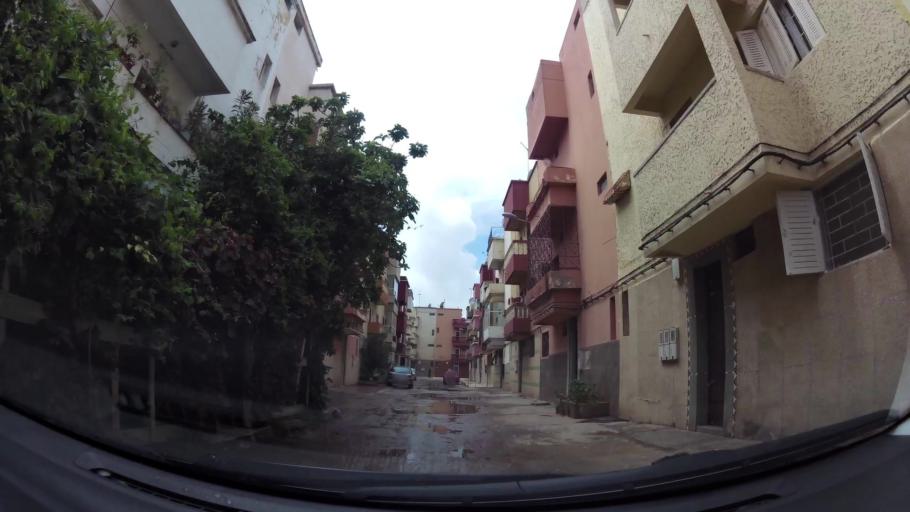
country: MA
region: Grand Casablanca
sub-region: Casablanca
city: Casablanca
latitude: 33.5517
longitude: -7.6865
